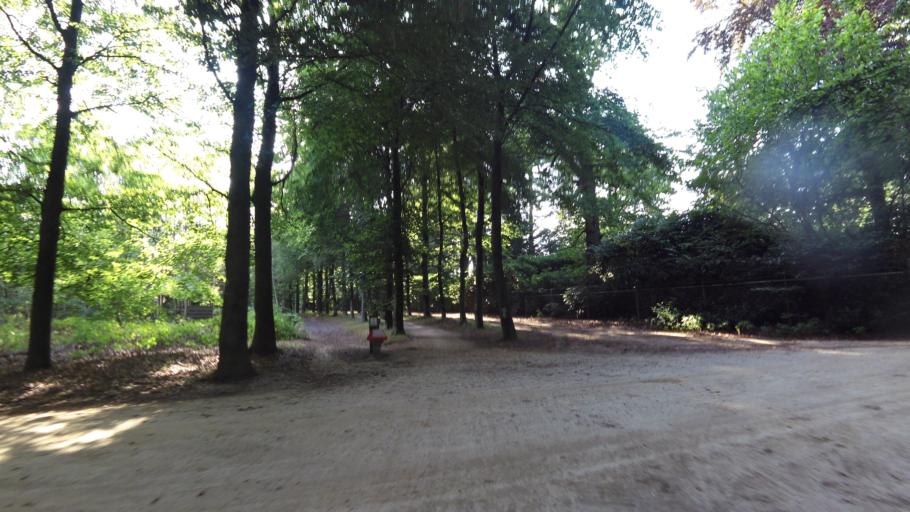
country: NL
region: Gelderland
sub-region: Gemeente Arnhem
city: Hoogkamp
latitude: 52.0189
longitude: 5.8608
